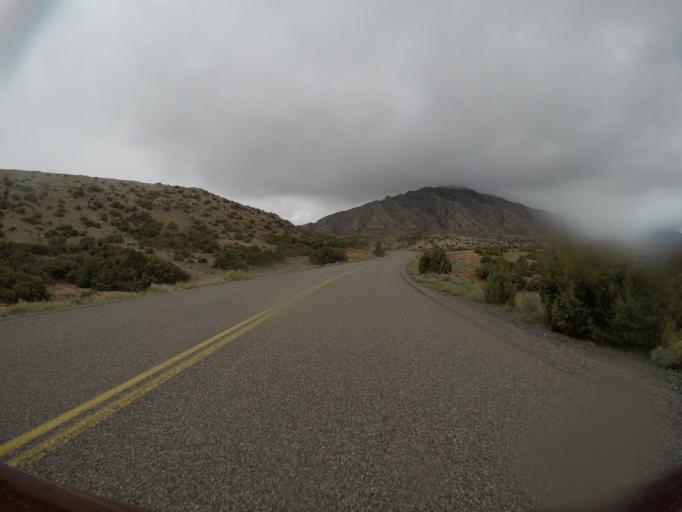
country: US
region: Wyoming
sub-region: Big Horn County
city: Lovell
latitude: 45.0249
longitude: -108.2584
